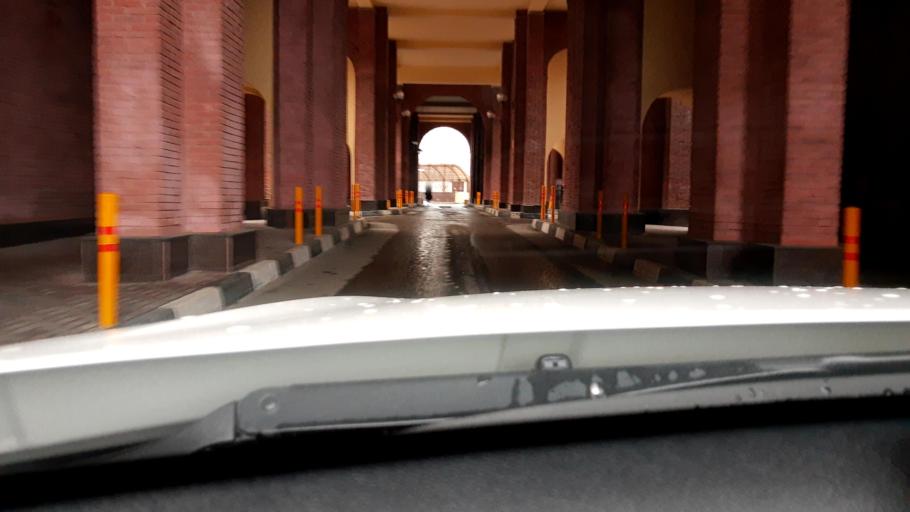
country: RU
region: Moscow
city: Sokol
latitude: 55.7979
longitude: 37.4959
